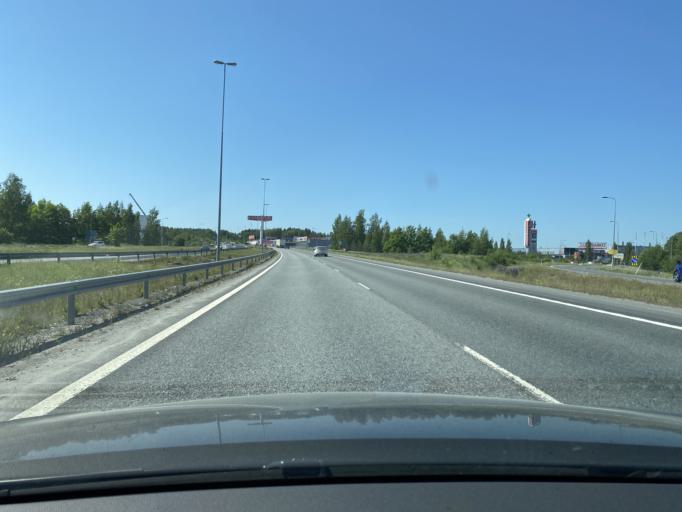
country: FI
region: Pirkanmaa
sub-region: Tampere
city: Tampere
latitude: 61.4628
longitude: 23.7289
